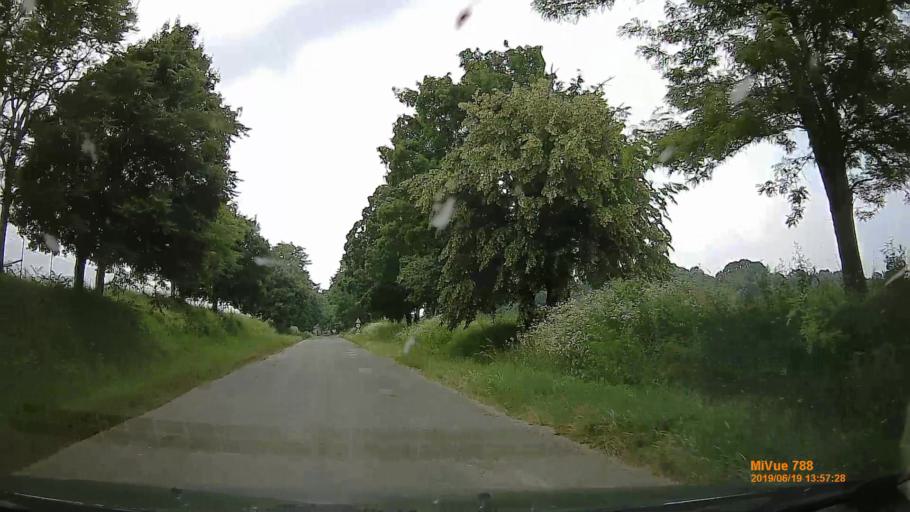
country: HU
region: Baranya
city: Szigetvar
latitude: 46.0854
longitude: 17.8012
